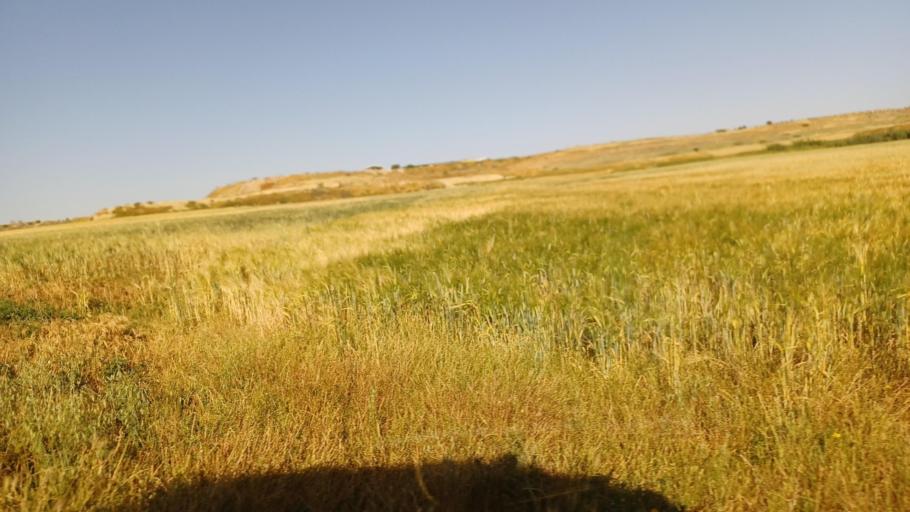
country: CY
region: Lefkosia
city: Mammari
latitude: 35.1565
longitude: 33.2433
